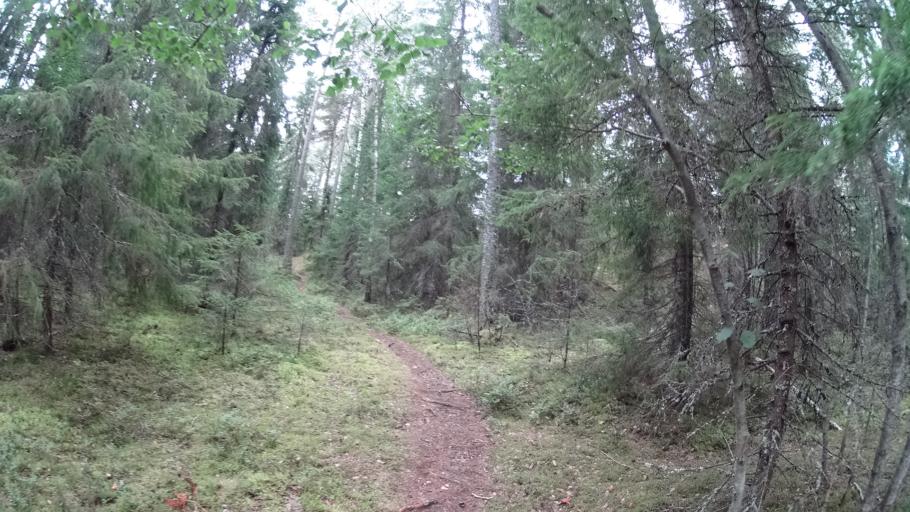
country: FI
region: Uusimaa
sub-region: Helsinki
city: Espoo
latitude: 60.3090
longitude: 24.5752
